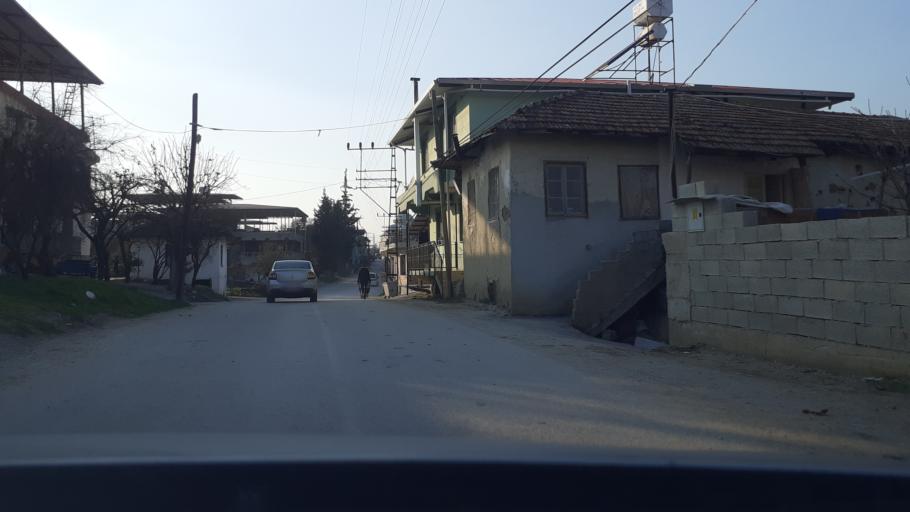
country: TR
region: Hatay
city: Oymakli
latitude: 36.1132
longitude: 36.2957
